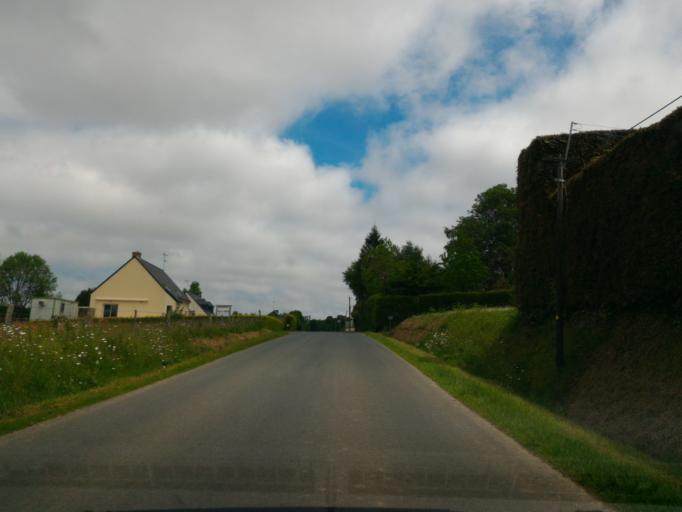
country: FR
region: Lower Normandy
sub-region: Departement de la Manche
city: Villedieu-les-Poeles
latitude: 48.8682
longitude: -1.1957
